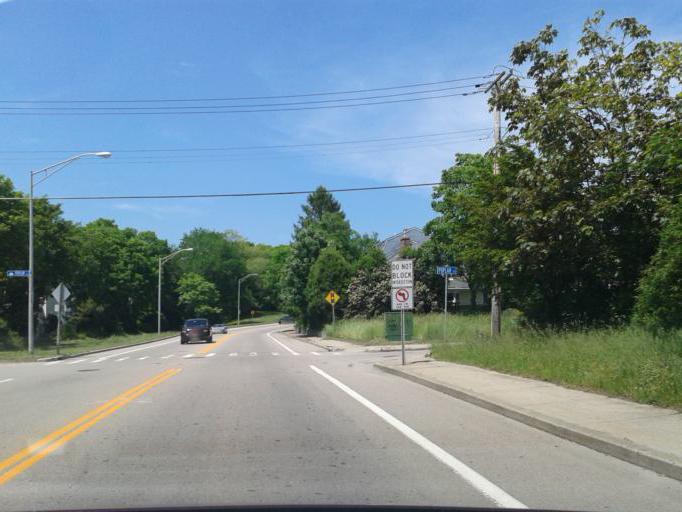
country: US
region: Rhode Island
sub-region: Newport County
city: Newport
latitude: 41.4932
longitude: -71.3174
